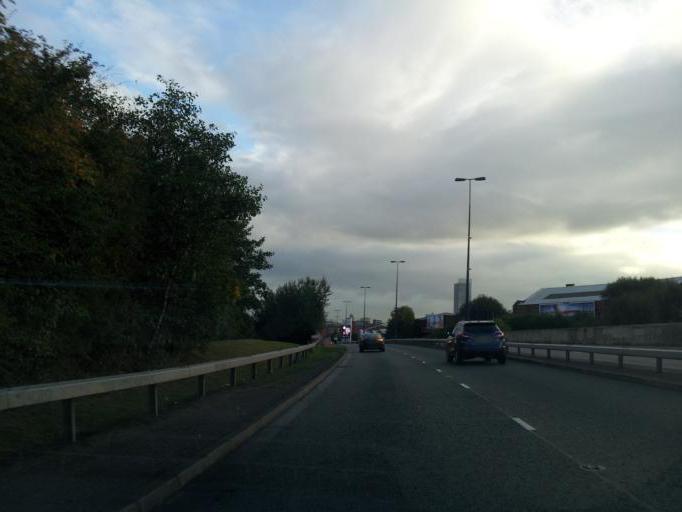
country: GB
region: England
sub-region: Manchester
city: Hulme
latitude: 53.4667
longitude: -2.2716
